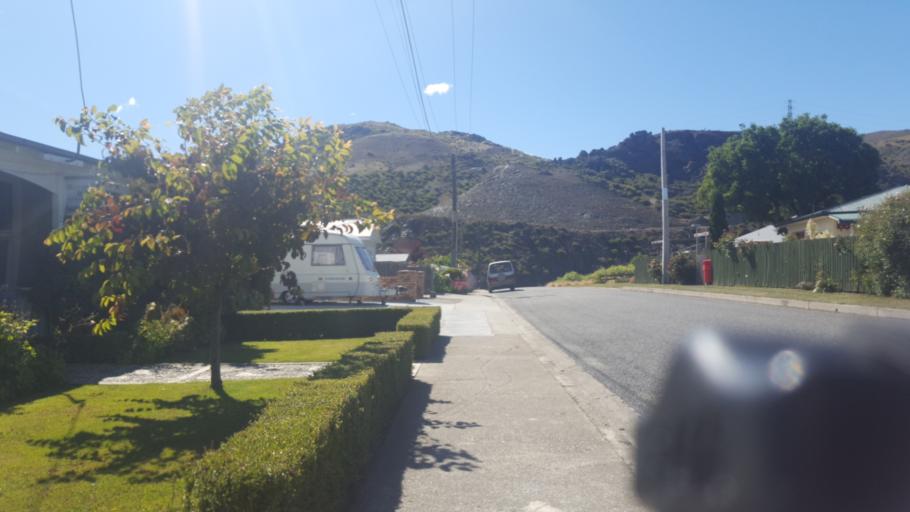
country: NZ
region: Otago
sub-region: Queenstown-Lakes District
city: Wanaka
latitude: -45.0477
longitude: 169.2106
